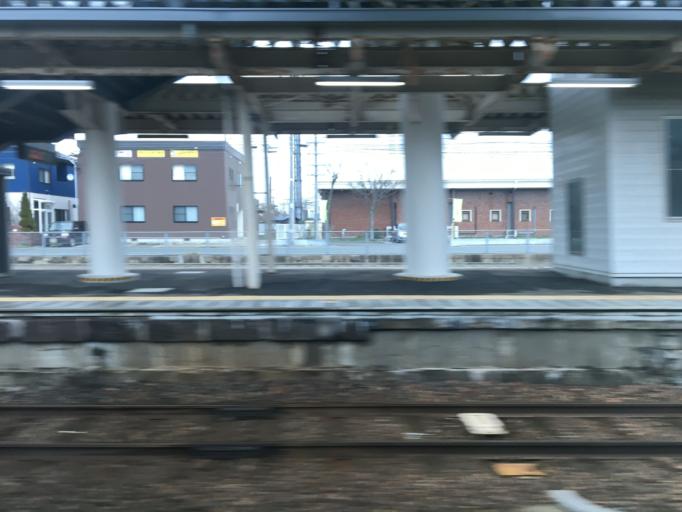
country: JP
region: Akita
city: Akita Shi
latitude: 39.7587
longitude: 140.0736
